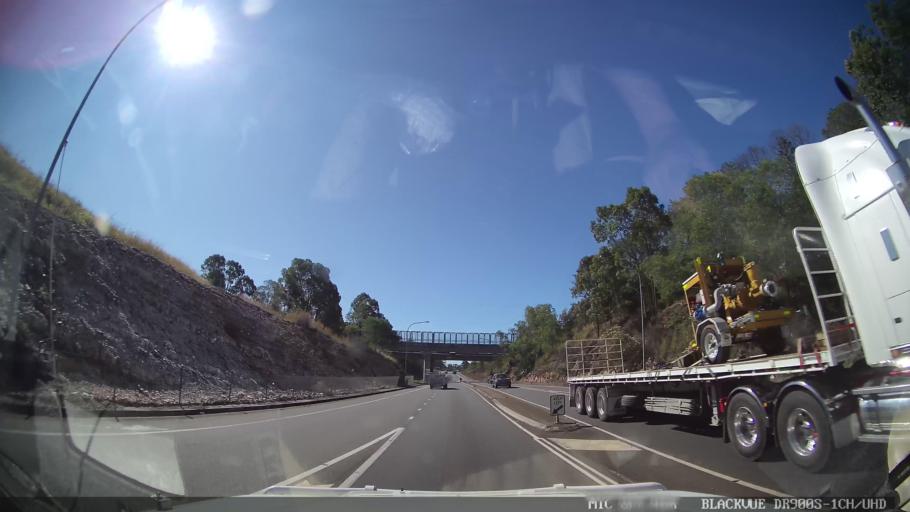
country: AU
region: Queensland
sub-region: Fraser Coast
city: Maryborough
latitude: -25.5183
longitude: 152.6693
